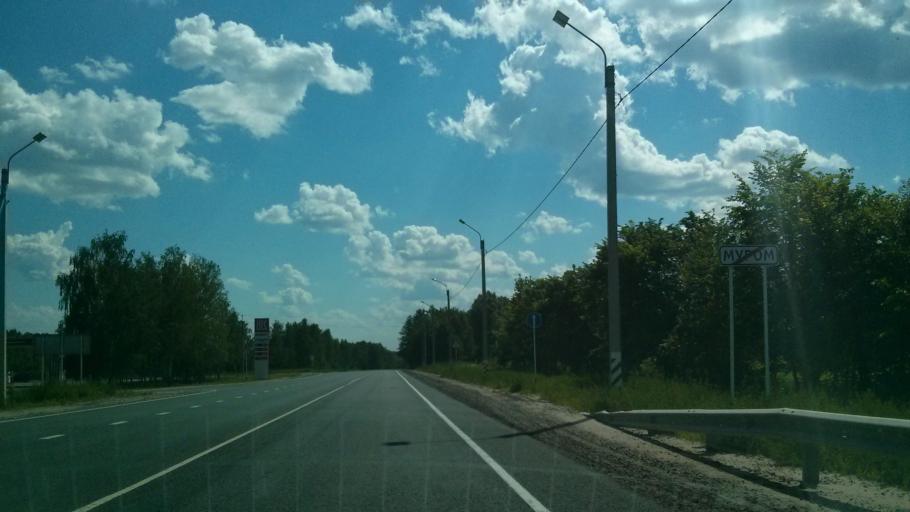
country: RU
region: Vladimir
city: Murom
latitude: 55.5289
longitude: 41.9563
